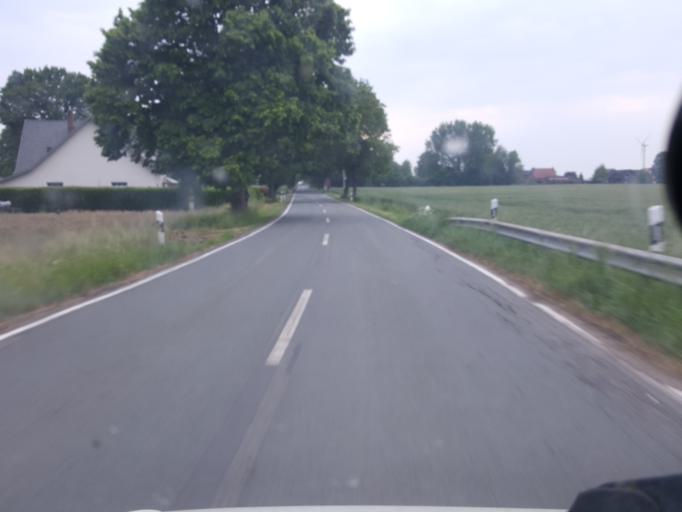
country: DE
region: Lower Saxony
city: Warmsen
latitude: 52.3706
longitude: 8.8751
